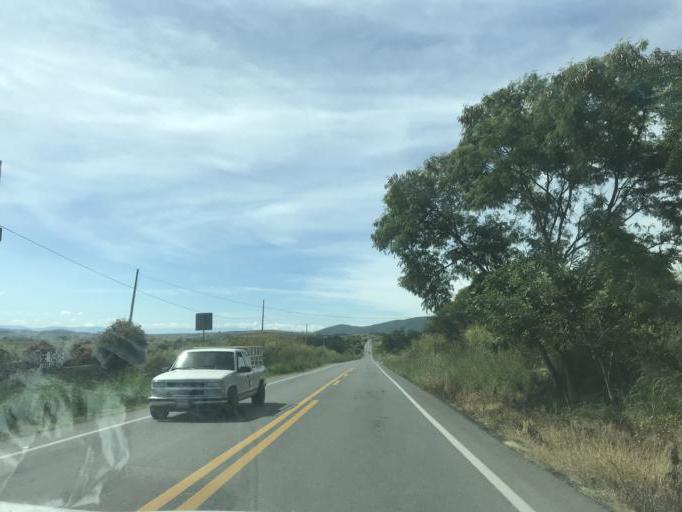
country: MX
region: Guerrero
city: Tepecoacuilco de Trujano
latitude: 18.2770
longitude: -99.5158
